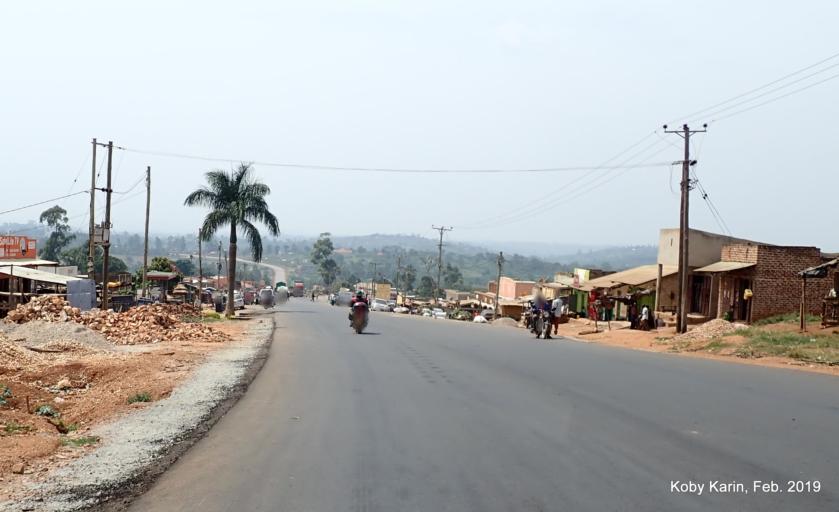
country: UG
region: Western Region
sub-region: Kyenjojo District
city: Kyenjojo
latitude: 0.6634
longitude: 30.5041
